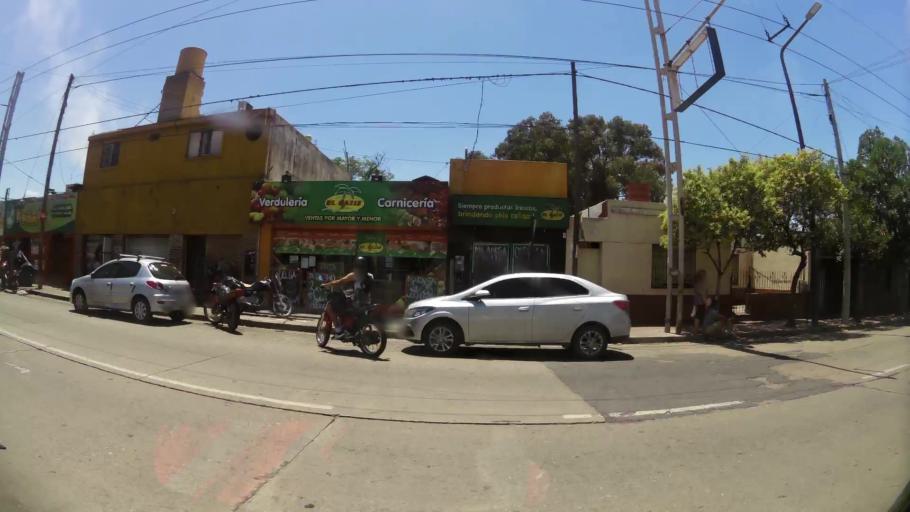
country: AR
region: Cordoba
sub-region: Departamento de Capital
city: Cordoba
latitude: -31.4015
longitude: -64.2236
